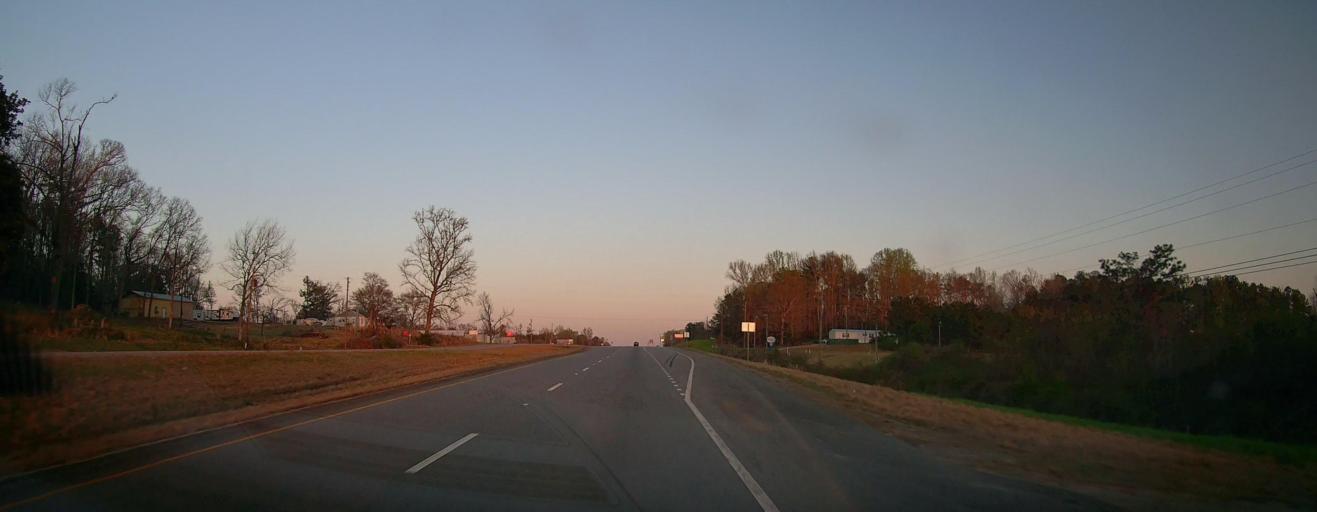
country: US
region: Alabama
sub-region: Tallapoosa County
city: Alexander City
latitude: 32.9746
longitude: -86.0330
